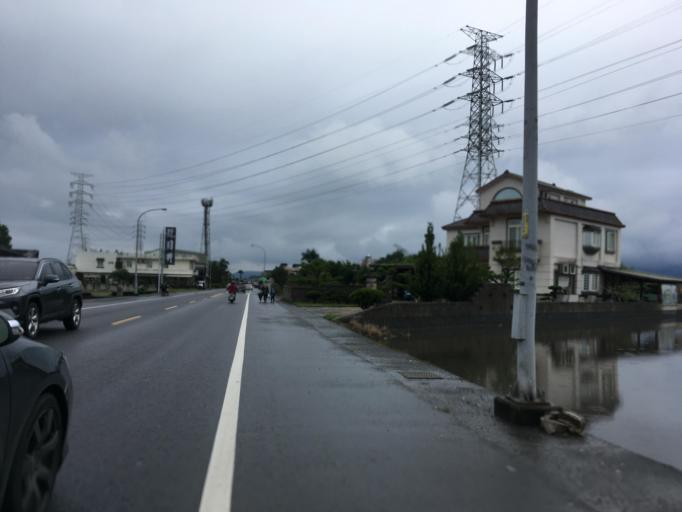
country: TW
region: Taiwan
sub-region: Yilan
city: Yilan
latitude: 24.6600
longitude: 121.7553
